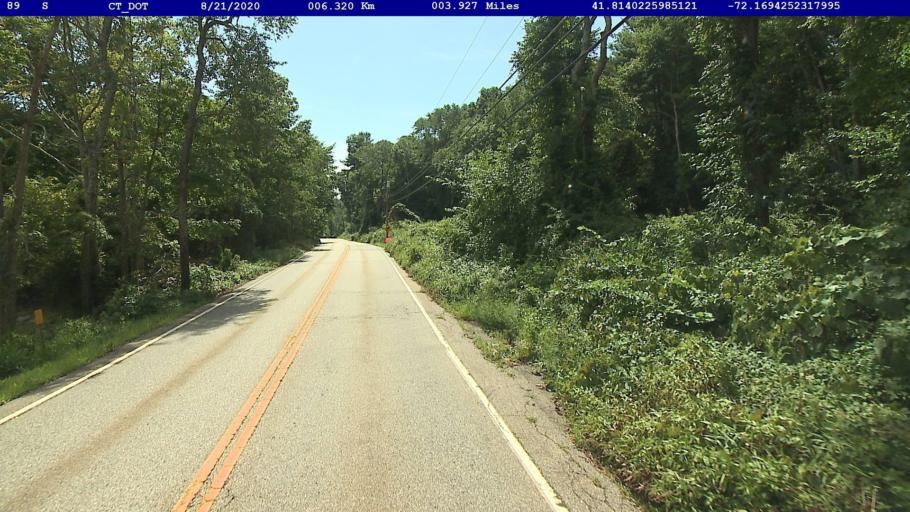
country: US
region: Connecticut
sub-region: Tolland County
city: Mansfield City
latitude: 41.8140
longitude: -72.1694
